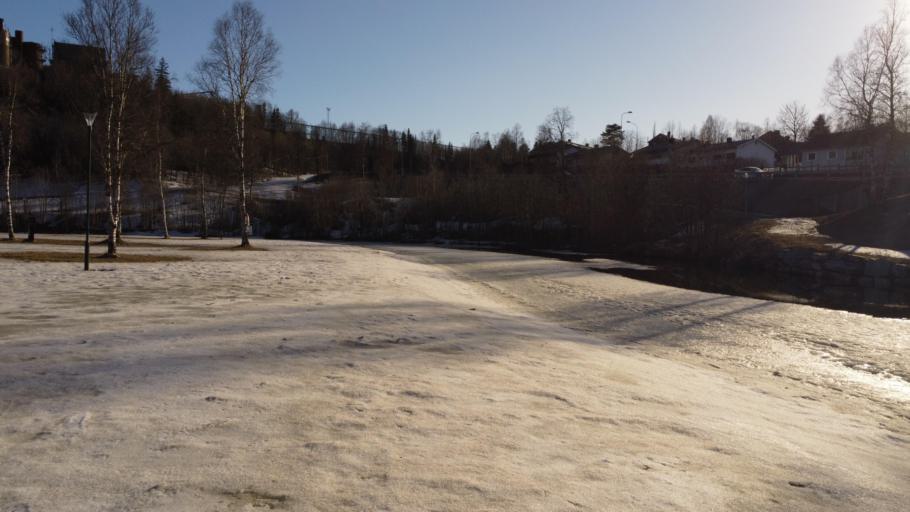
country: NO
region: Nordland
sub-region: Rana
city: Mo i Rana
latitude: 66.3162
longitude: 14.1697
